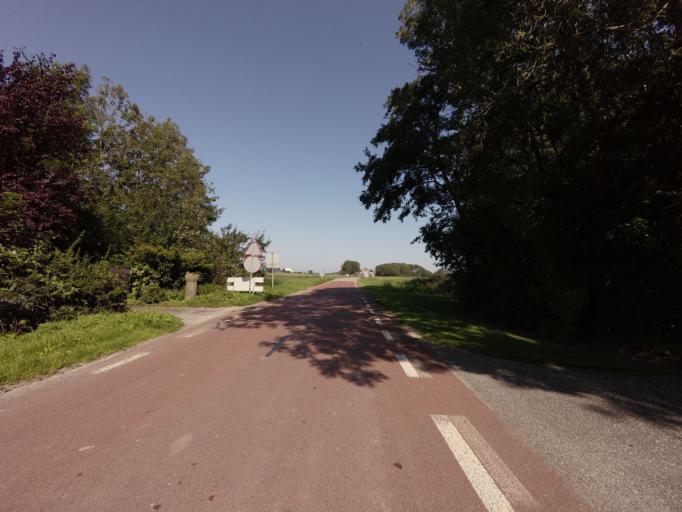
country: NL
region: Friesland
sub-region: Gemeente Dongeradeel
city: Ternaard
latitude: 53.3633
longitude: 5.9810
